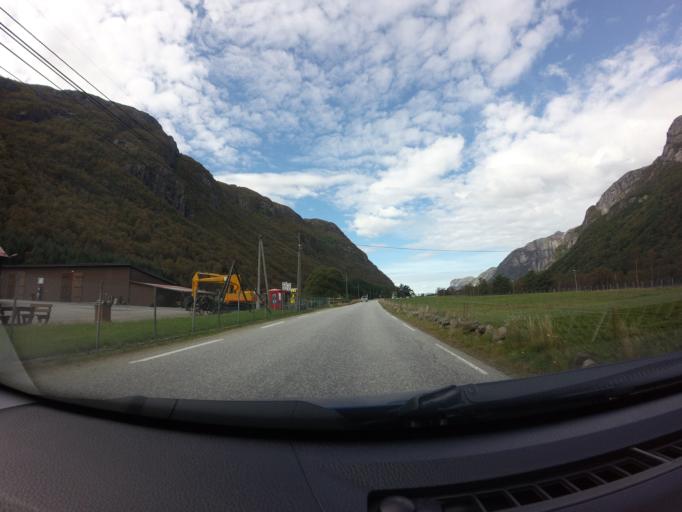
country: NO
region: Rogaland
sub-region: Forsand
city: Forsand
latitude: 58.8218
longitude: 6.2000
